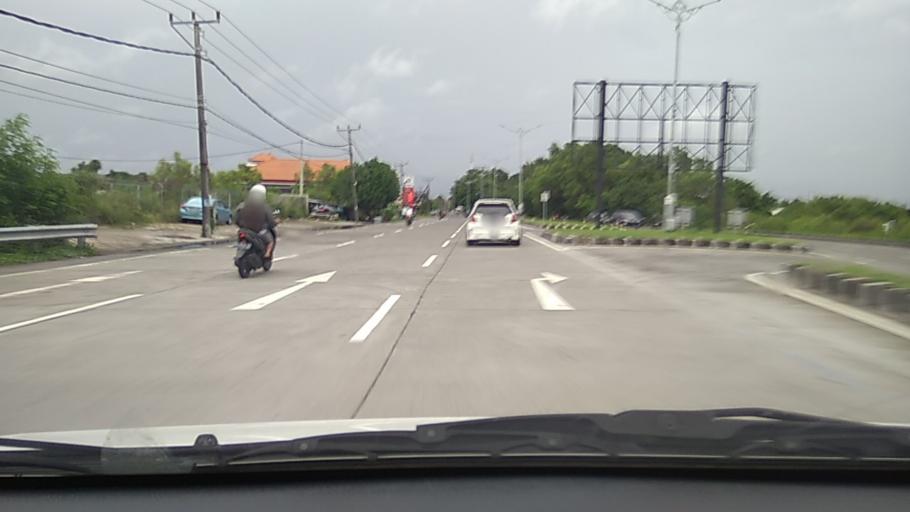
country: ID
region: Bali
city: Karyadharma
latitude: -8.7238
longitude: 115.2141
